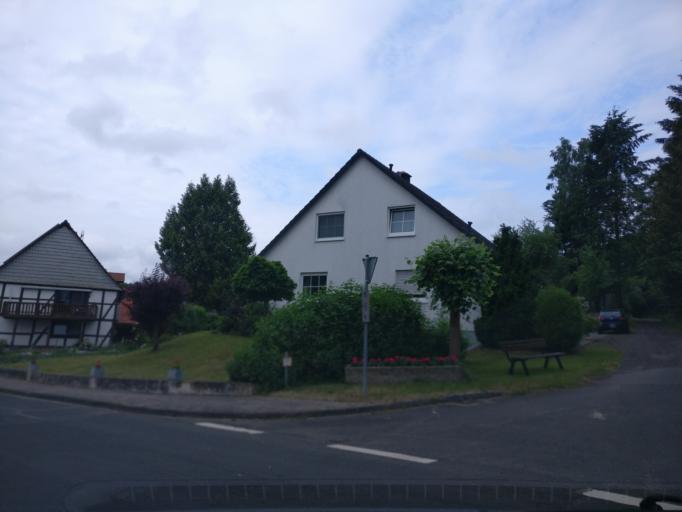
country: DE
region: Lower Saxony
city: Scheden
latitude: 51.4270
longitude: 9.7148
